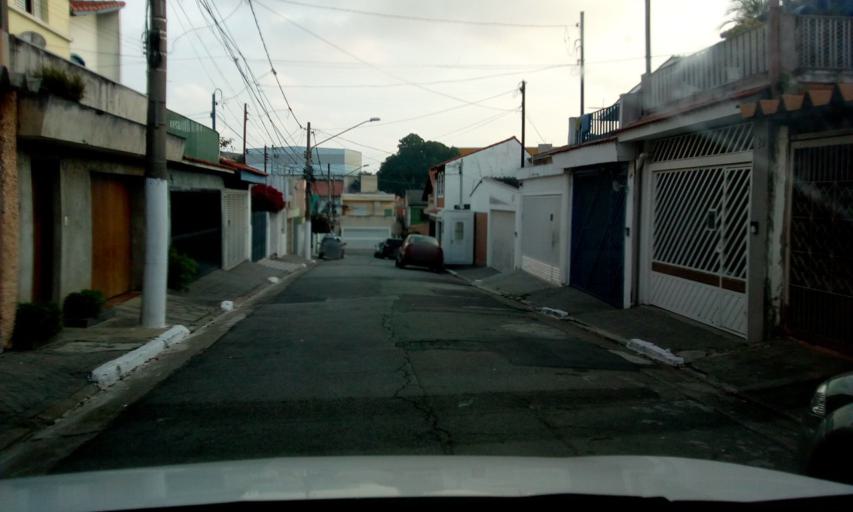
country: BR
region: Sao Paulo
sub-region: Diadema
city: Diadema
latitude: -23.6209
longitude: -46.6524
